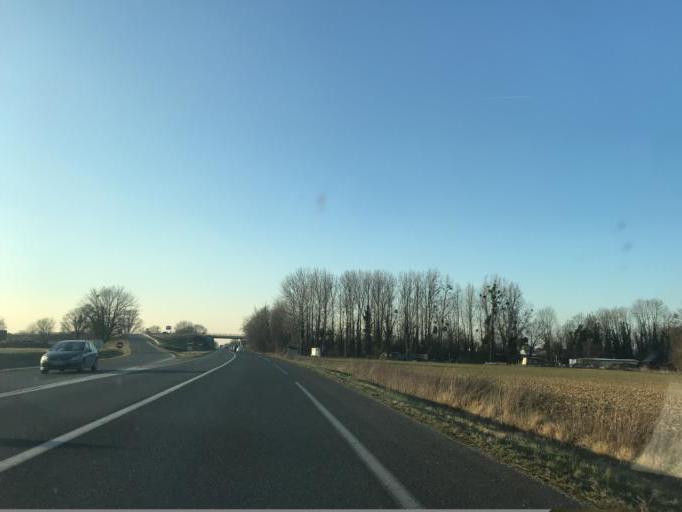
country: FR
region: Ile-de-France
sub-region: Departement de Seine-et-Marne
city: Villiers-sur-Morin
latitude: 48.8543
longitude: 2.8598
